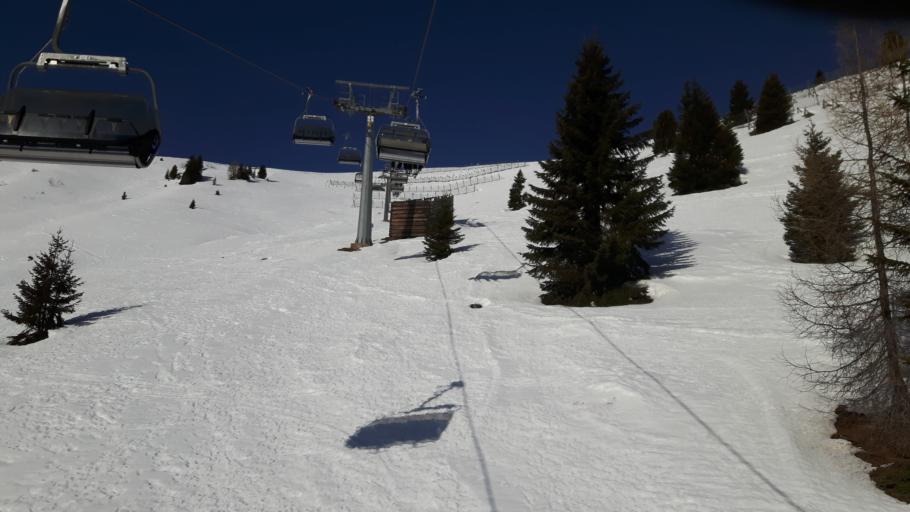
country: IT
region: Trentino-Alto Adige
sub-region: Provincia di Trento
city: Predazzo
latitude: 46.3446
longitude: 11.5647
